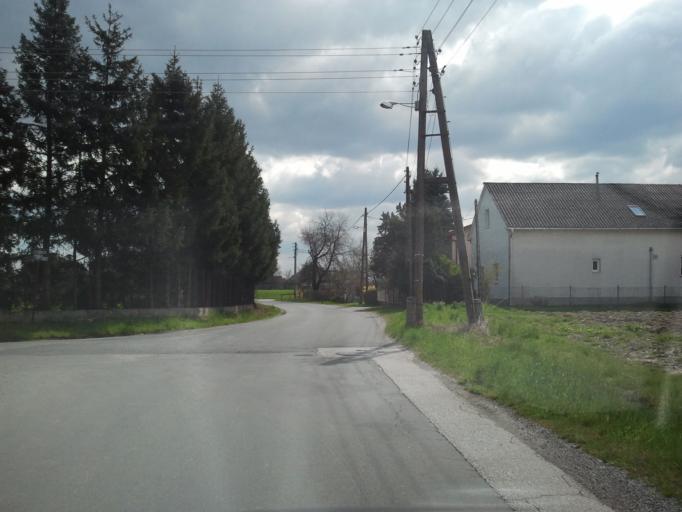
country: HR
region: Grad Zagreb
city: Brezovica
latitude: 45.7390
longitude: 15.8824
